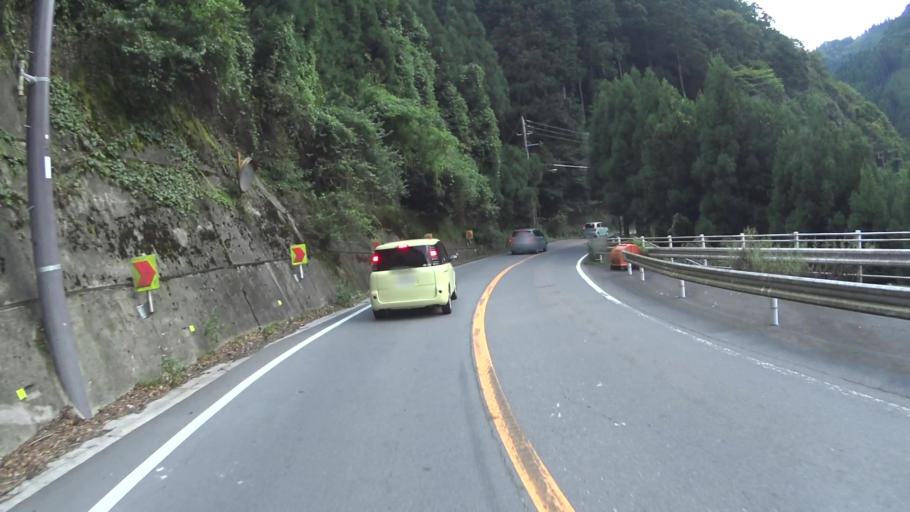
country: JP
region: Kyoto
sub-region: Kyoto-shi
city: Kamigyo-ku
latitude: 35.0717
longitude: 135.6856
